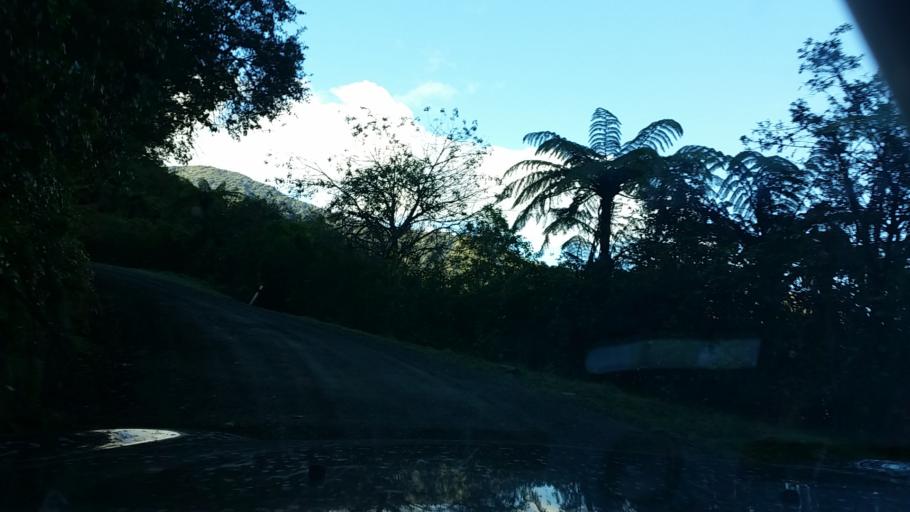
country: NZ
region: Marlborough
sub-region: Marlborough District
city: Picton
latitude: -41.1399
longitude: 174.0472
